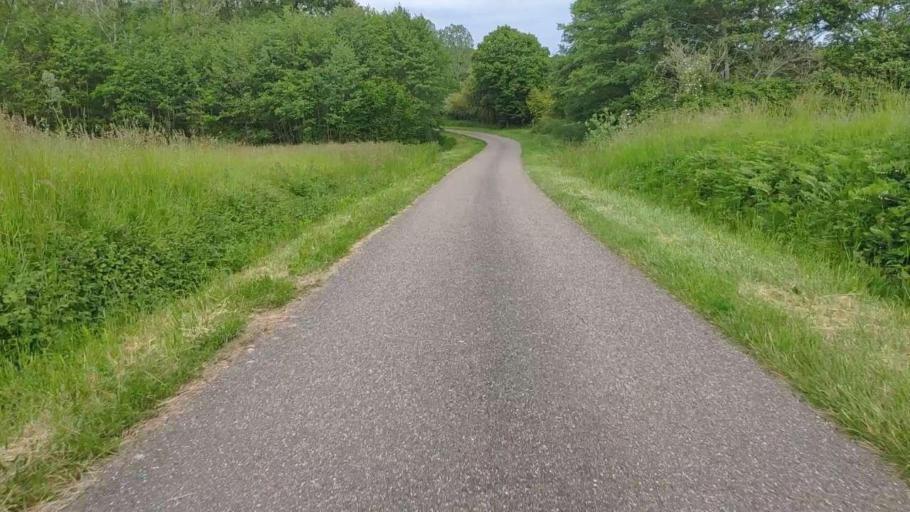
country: FR
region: Bourgogne
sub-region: Departement de Saone-et-Loire
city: Saint-Germain-du-Bois
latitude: 46.7977
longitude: 5.3456
